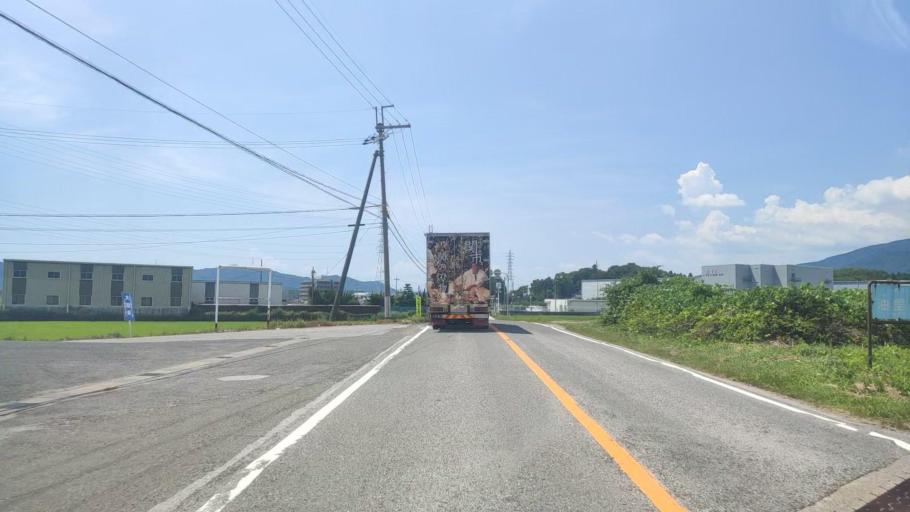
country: JP
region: Shiga Prefecture
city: Nagahama
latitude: 35.3826
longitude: 136.3709
